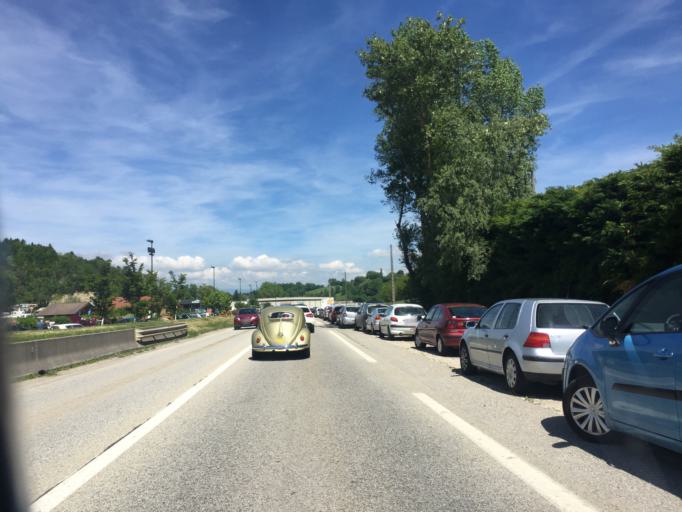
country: FR
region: Rhone-Alpes
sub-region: Departement de la Haute-Savoie
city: La Balme-de-Sillingy
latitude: 45.9695
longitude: 6.0338
